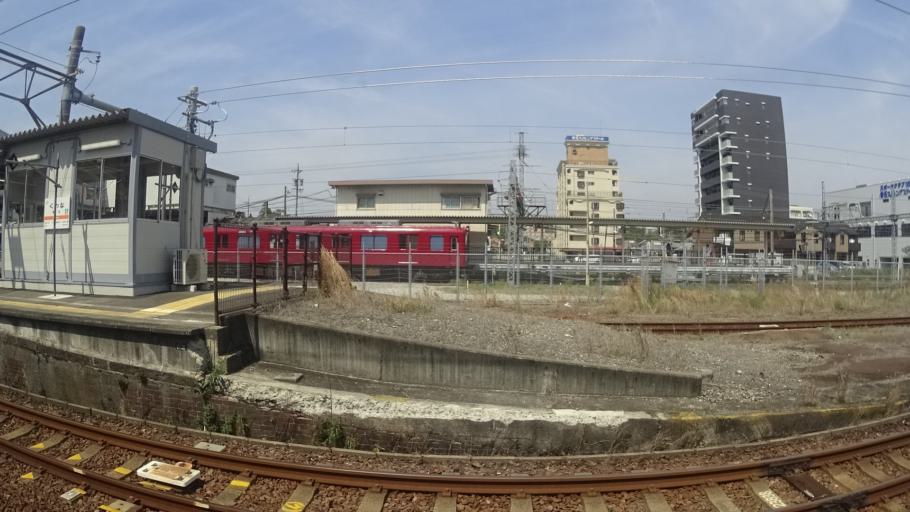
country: JP
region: Aichi
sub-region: Tsushima-shi
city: Tsushima
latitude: 35.0677
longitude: 136.6839
